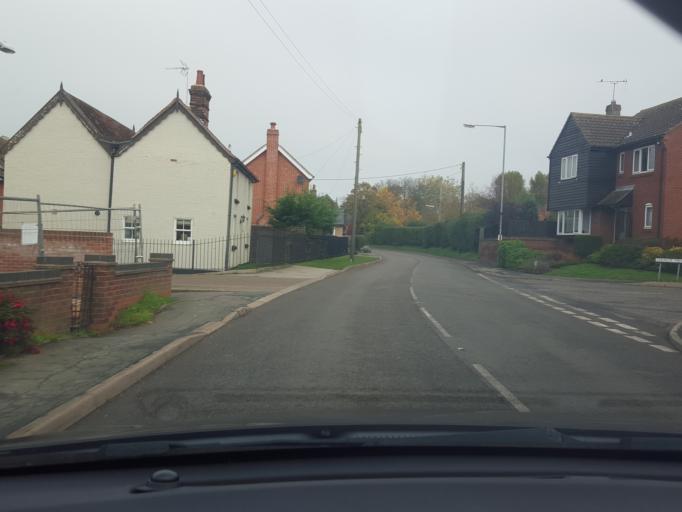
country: GB
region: England
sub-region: Suffolk
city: East Bergholt
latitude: 51.9248
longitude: 0.9848
